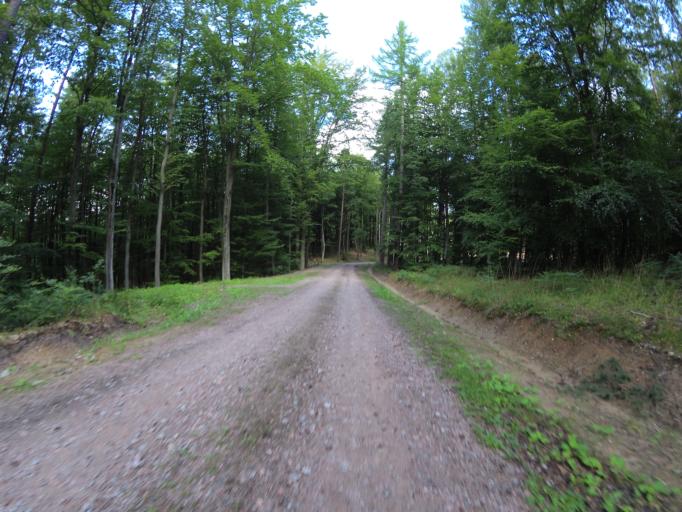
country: PL
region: Pomeranian Voivodeship
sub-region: Powiat wejherowski
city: Bojano
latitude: 54.5168
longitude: 18.4249
